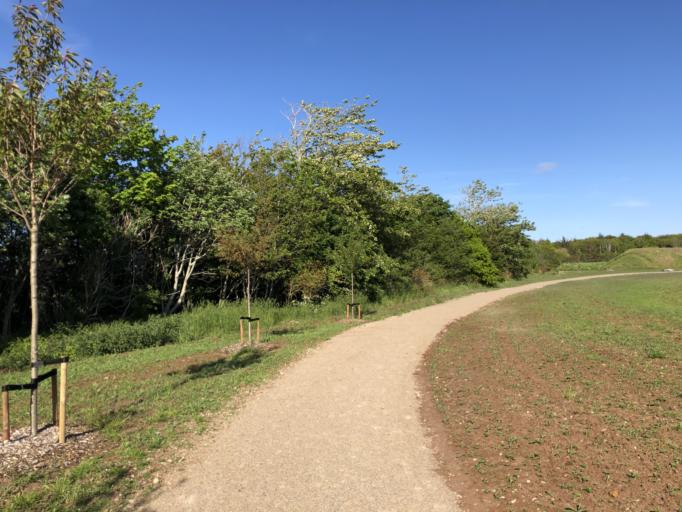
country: DK
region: Central Jutland
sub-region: Holstebro Kommune
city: Ulfborg
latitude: 56.2790
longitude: 8.3097
